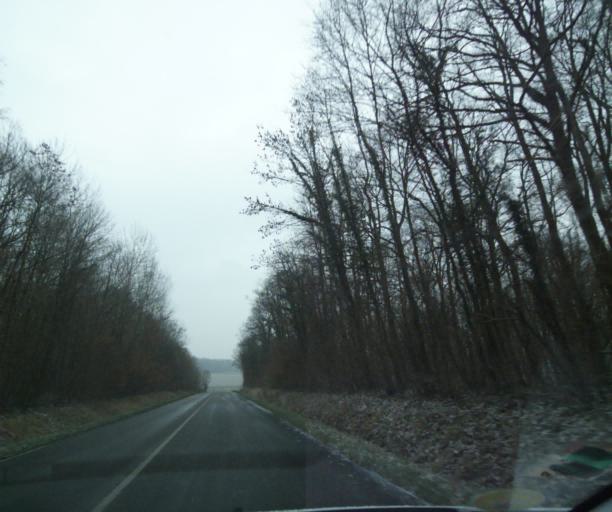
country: FR
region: Champagne-Ardenne
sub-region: Departement de la Haute-Marne
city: Wassy
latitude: 48.4720
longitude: 5.0213
